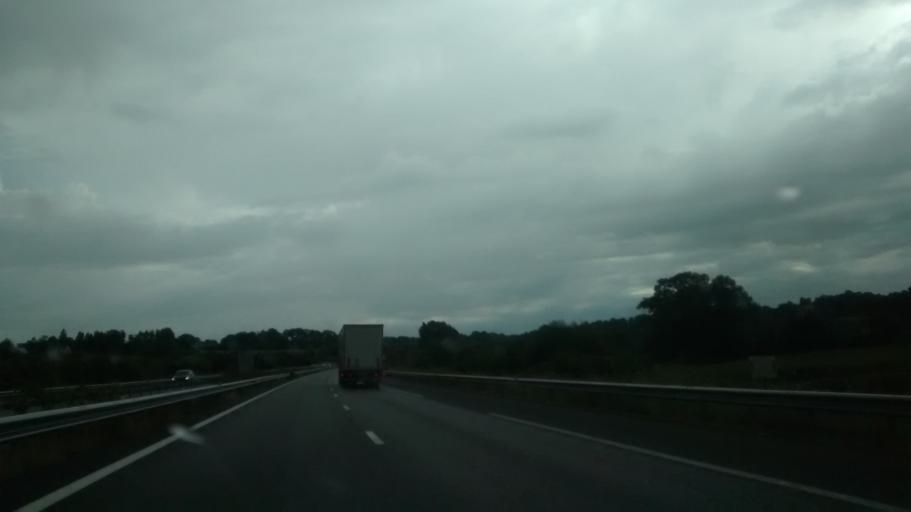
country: FR
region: Brittany
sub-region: Departement d'Ille-et-Vilaine
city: Saint-Jean-sur-Couesnon
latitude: 48.2976
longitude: -1.3644
